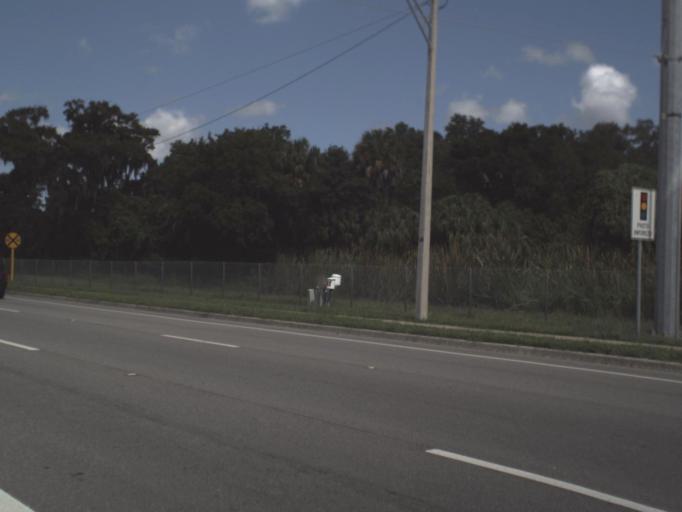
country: US
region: Florida
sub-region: Pinellas County
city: Oldsmar
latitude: 28.0378
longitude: -82.6606
